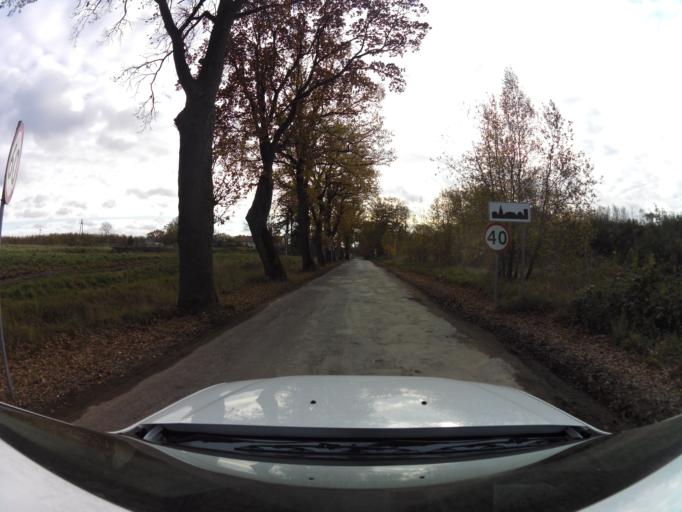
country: PL
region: West Pomeranian Voivodeship
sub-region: Powiat gryficki
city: Gryfice
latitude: 53.9336
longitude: 15.1903
